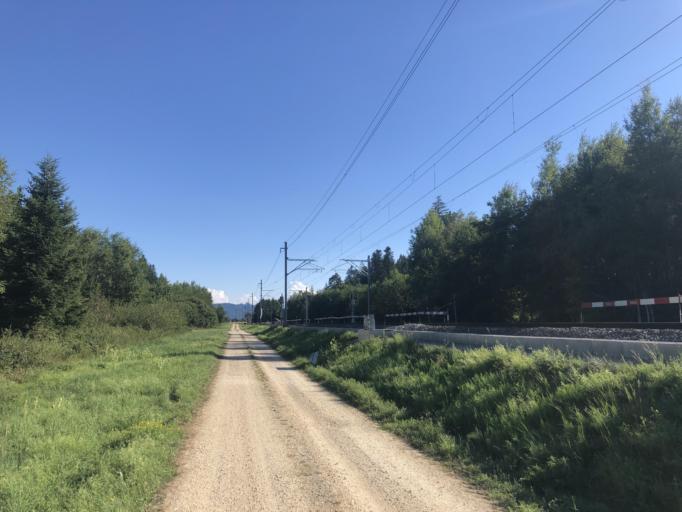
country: CH
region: Bern
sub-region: Bern-Mittelland District
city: Jegenstorf
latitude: 47.0662
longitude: 7.5071
